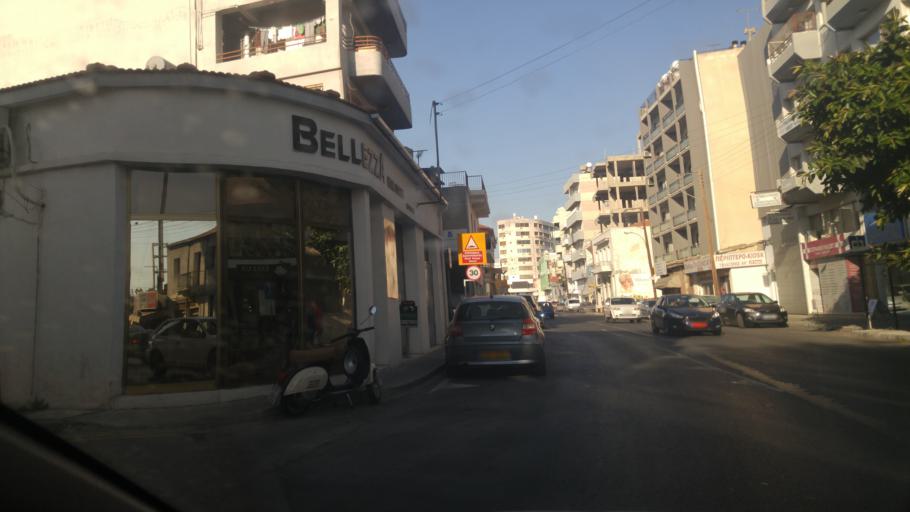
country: CY
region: Limassol
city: Limassol
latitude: 34.6791
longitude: 33.0416
